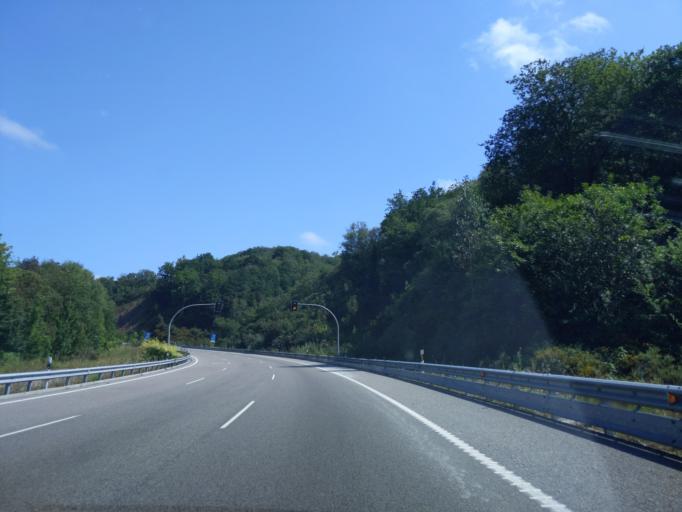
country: ES
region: Asturias
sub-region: Province of Asturias
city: Sama
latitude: 43.3362
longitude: -5.7070
